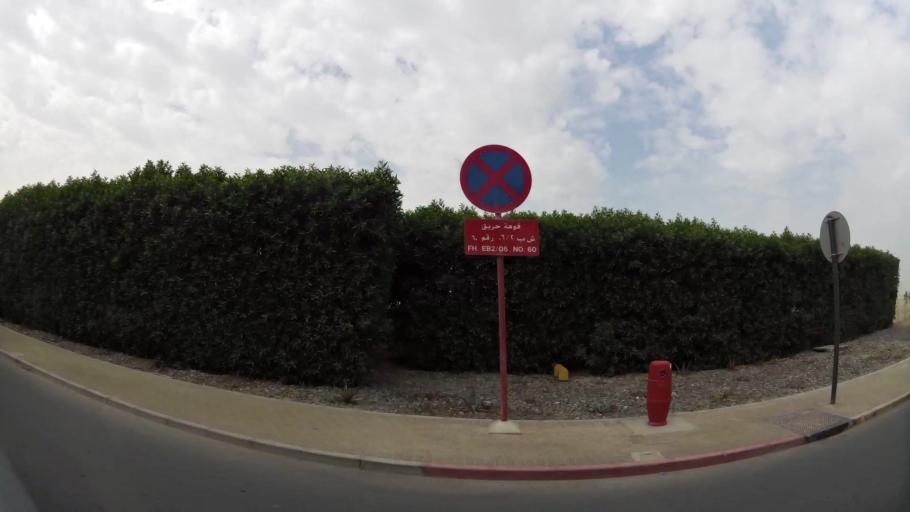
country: AE
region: Abu Dhabi
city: Abu Dhabi
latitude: 24.3114
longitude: 54.6179
